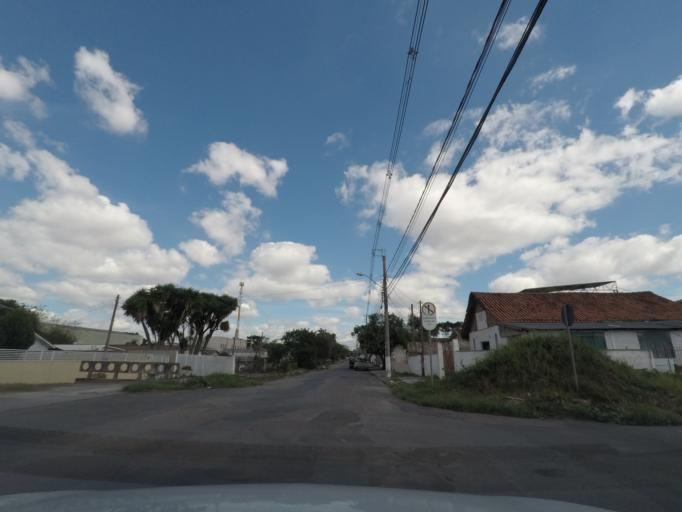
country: BR
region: Parana
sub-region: Sao Jose Dos Pinhais
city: Sao Jose dos Pinhais
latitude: -25.4997
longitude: -49.2287
